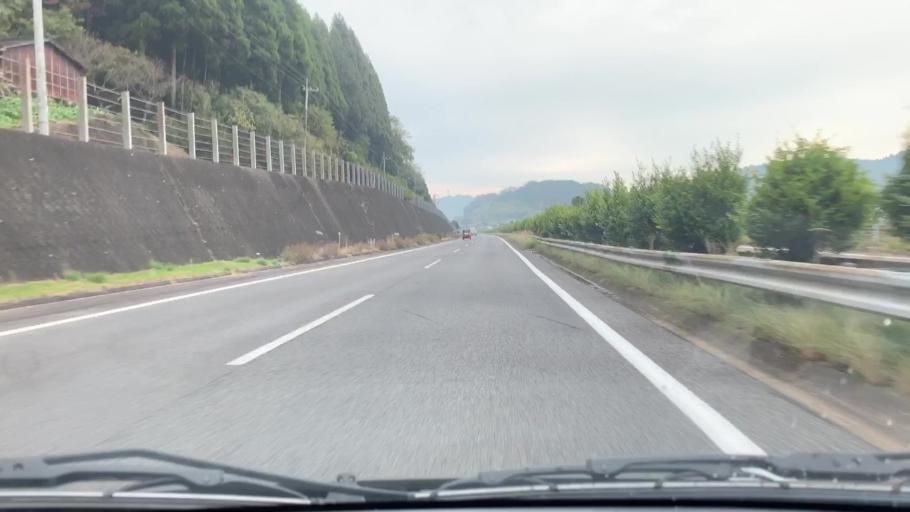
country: JP
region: Saga Prefecture
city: Takeocho-takeo
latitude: 33.2712
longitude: 130.1011
